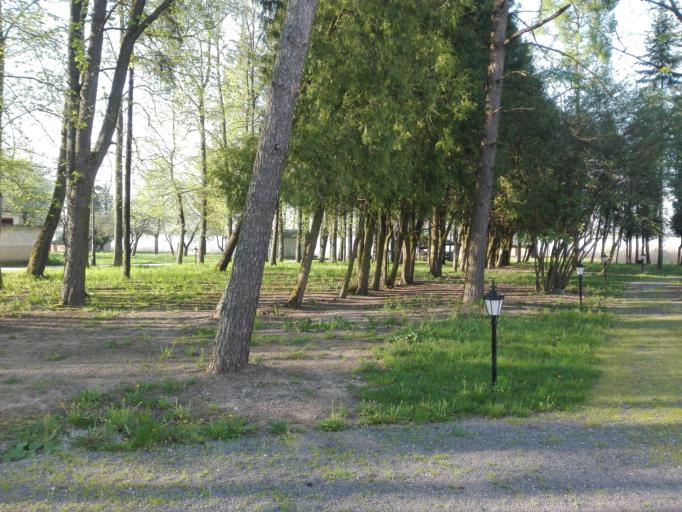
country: LT
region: Vilnius County
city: Ukmerge
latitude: 55.4252
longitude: 24.5633
